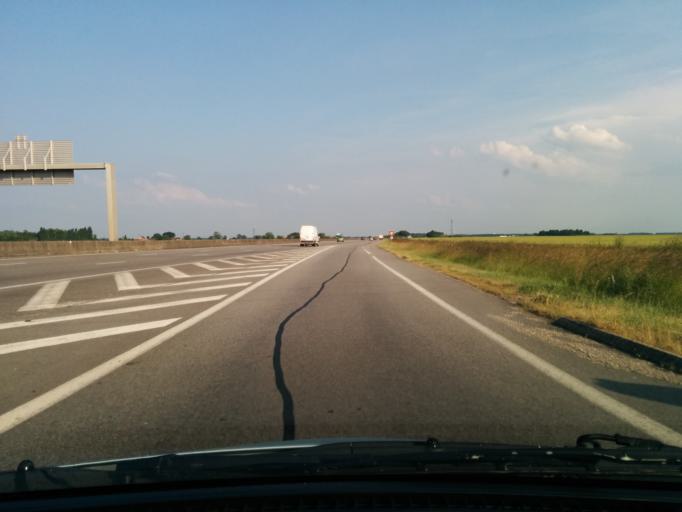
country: FR
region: Haute-Normandie
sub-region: Departement de l'Eure
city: Saint-Aubin-sur-Gaillon
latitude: 49.1328
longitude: 1.3161
